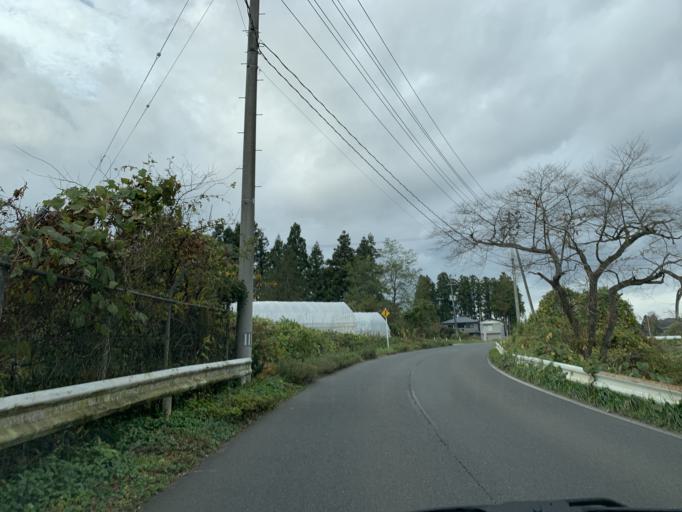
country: JP
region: Iwate
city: Mizusawa
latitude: 39.0535
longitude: 141.1118
